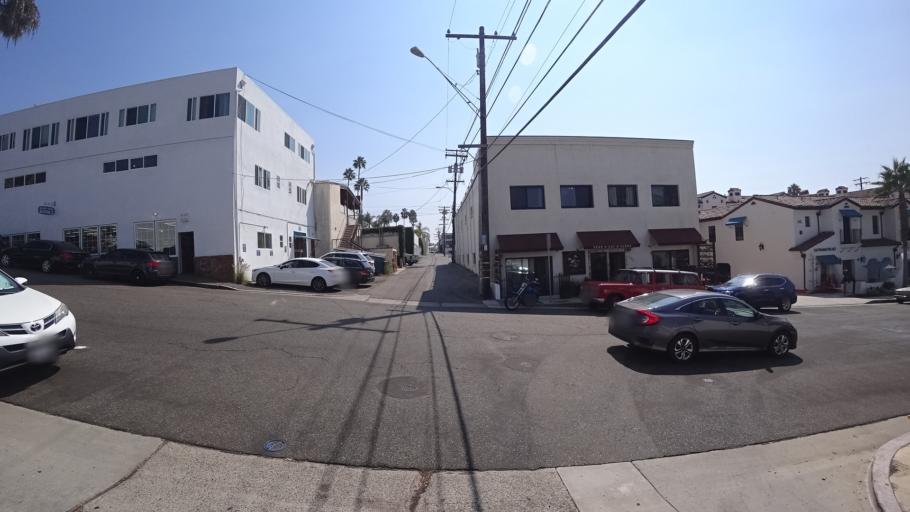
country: US
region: California
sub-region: Orange County
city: San Clemente
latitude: 33.4285
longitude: -117.6141
